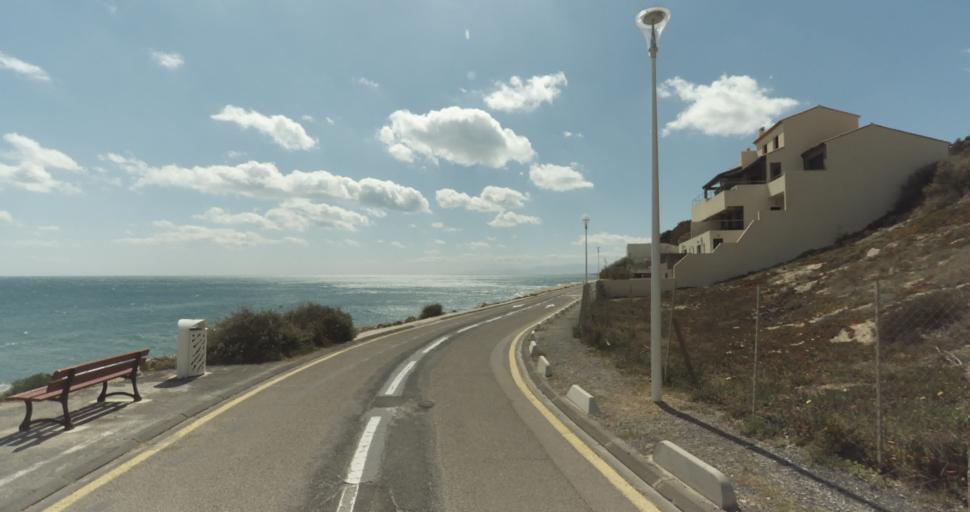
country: FR
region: Languedoc-Roussillon
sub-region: Departement de l'Aude
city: Leucate
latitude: 42.9100
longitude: 3.0579
